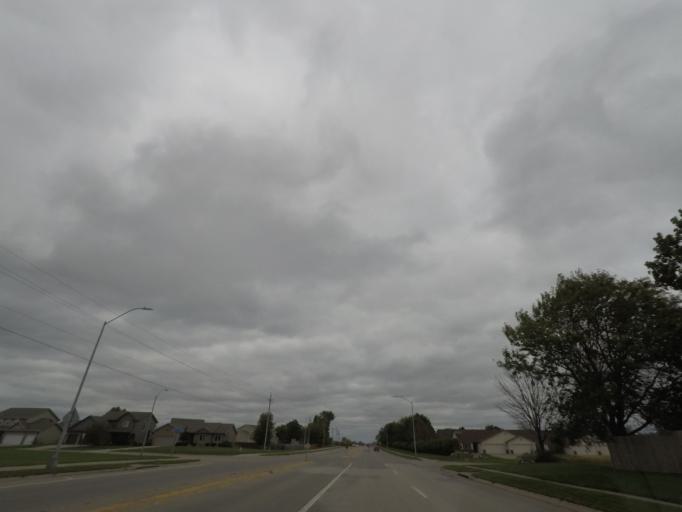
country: US
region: Iowa
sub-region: Polk County
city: Saylorville
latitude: 41.6955
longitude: -93.6005
